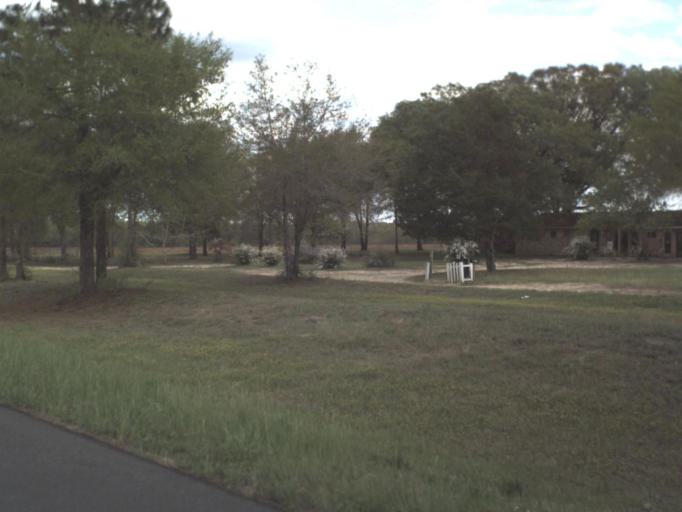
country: US
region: Florida
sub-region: Okaloosa County
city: Crestview
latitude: 30.8763
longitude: -86.5151
